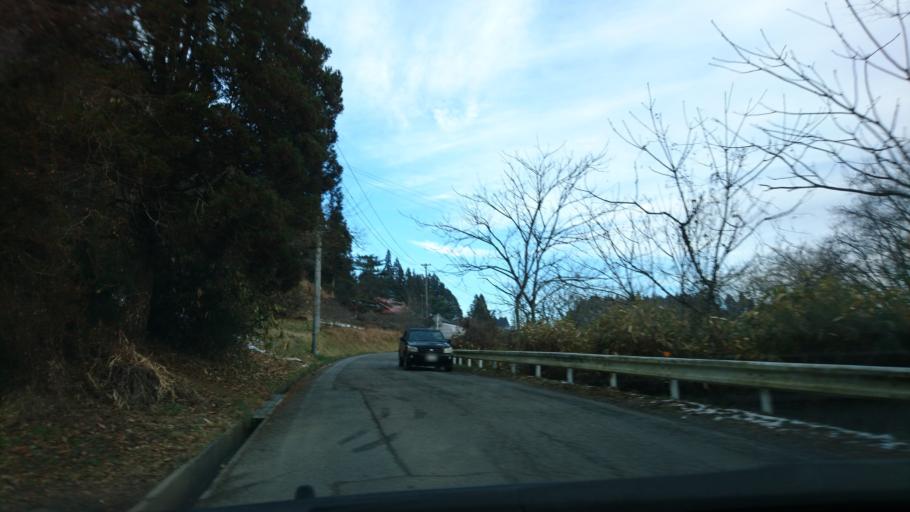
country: JP
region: Iwate
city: Ichinoseki
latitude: 38.9061
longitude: 141.3328
